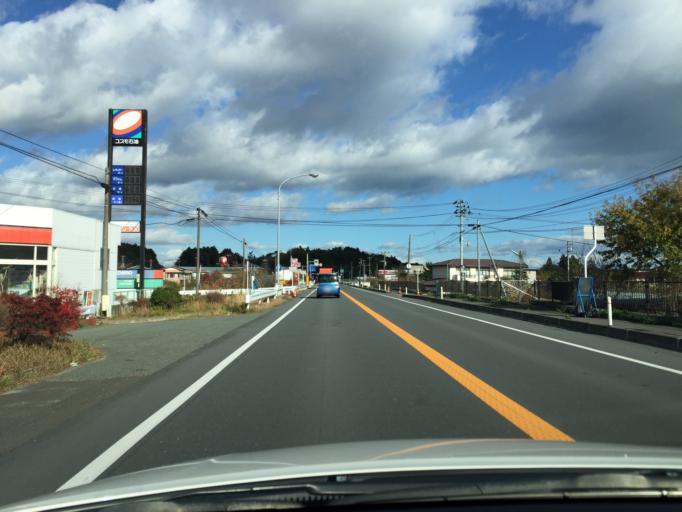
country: JP
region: Fukushima
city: Namie
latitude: 37.4549
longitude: 141.0099
